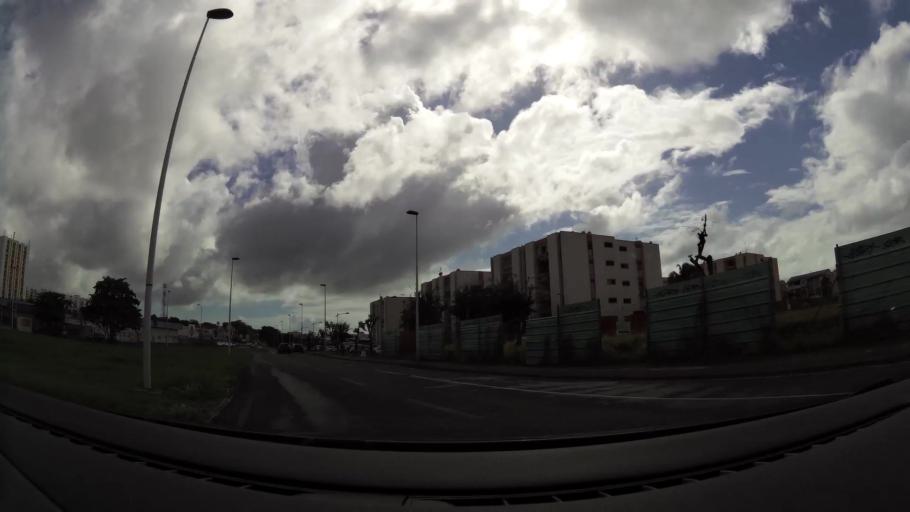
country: GP
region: Guadeloupe
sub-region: Guadeloupe
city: Pointe-a-Pitre
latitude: 16.2503
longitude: -61.5425
